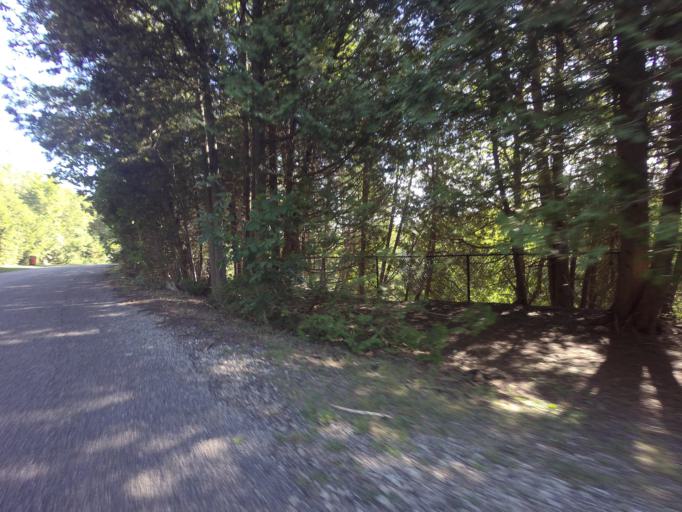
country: CA
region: Ontario
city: Waterloo
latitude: 43.6753
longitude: -80.4487
